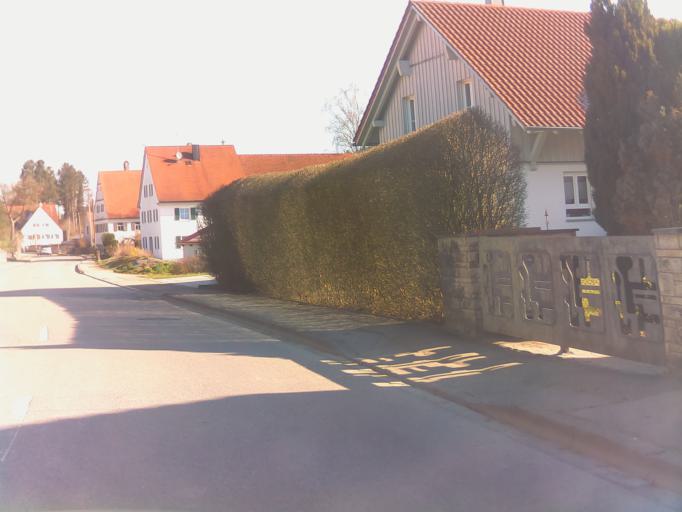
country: DE
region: Bavaria
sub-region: Swabia
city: Fischach
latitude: 48.2744
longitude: 10.7030
